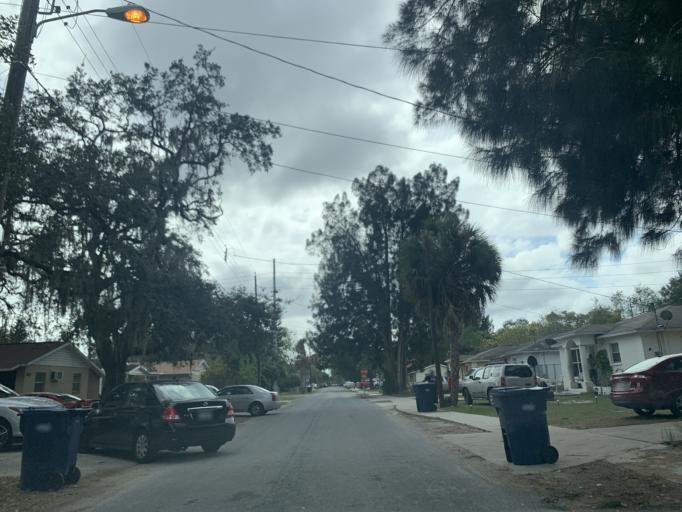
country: US
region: Florida
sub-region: Hillsborough County
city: East Lake-Orient Park
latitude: 27.9785
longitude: -82.3970
